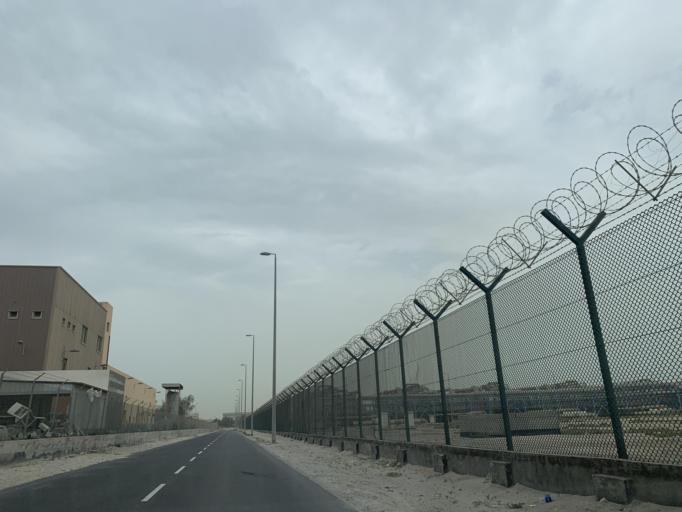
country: BH
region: Muharraq
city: Al Hadd
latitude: 26.2232
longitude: 50.6664
